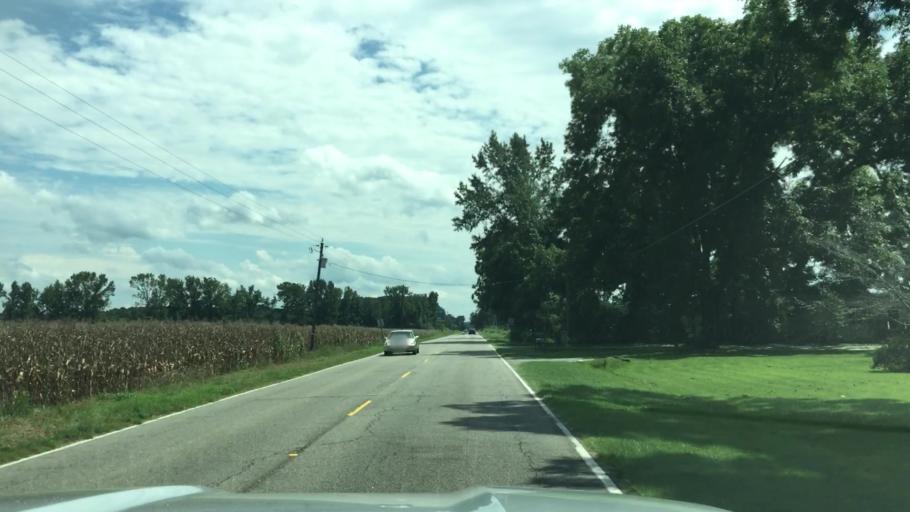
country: US
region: South Carolina
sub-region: Darlington County
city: Hartsville
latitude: 34.3471
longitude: -80.0536
